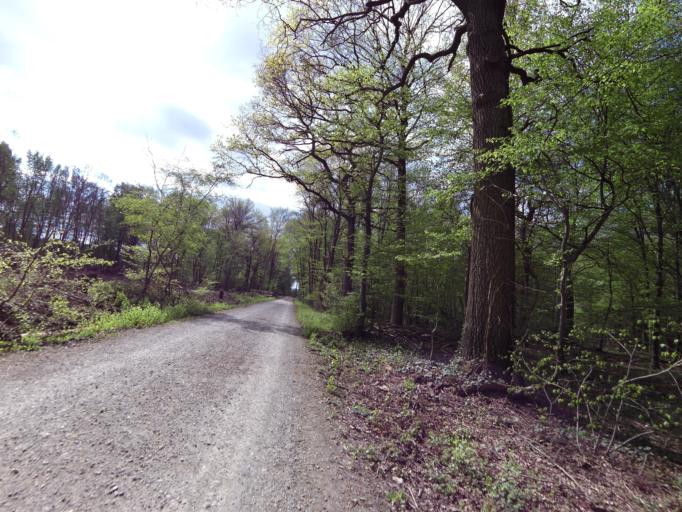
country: DE
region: North Rhine-Westphalia
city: Meckenheim
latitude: 50.6673
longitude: 7.0343
